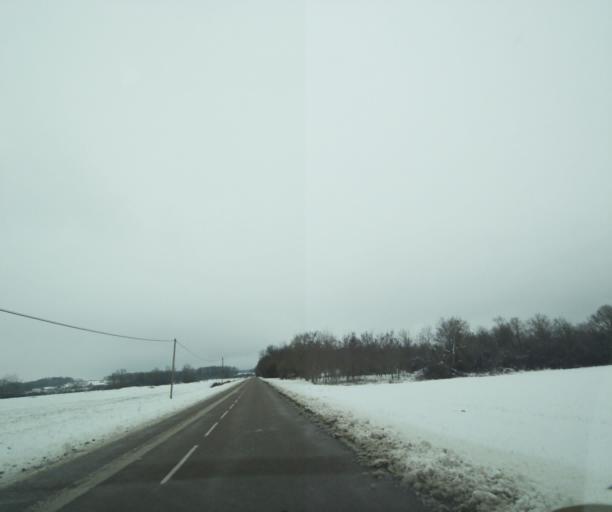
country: FR
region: Champagne-Ardenne
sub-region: Departement de la Haute-Marne
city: Montier-en-Der
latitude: 48.4499
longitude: 4.7807
